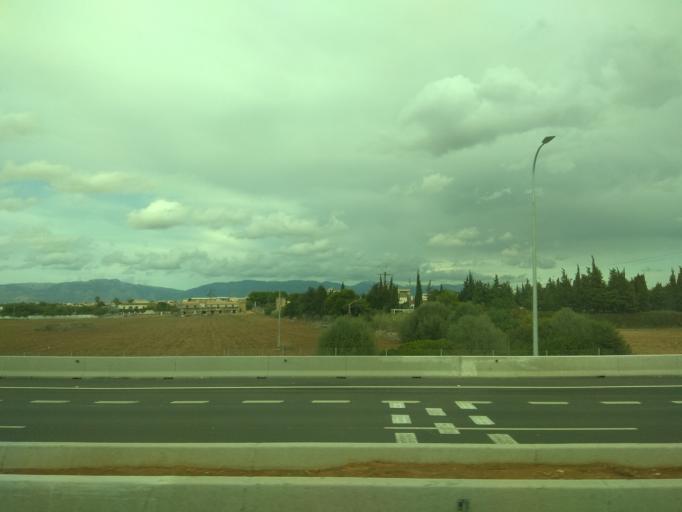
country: ES
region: Balearic Islands
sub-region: Illes Balears
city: Palma
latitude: 39.5680
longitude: 2.7126
